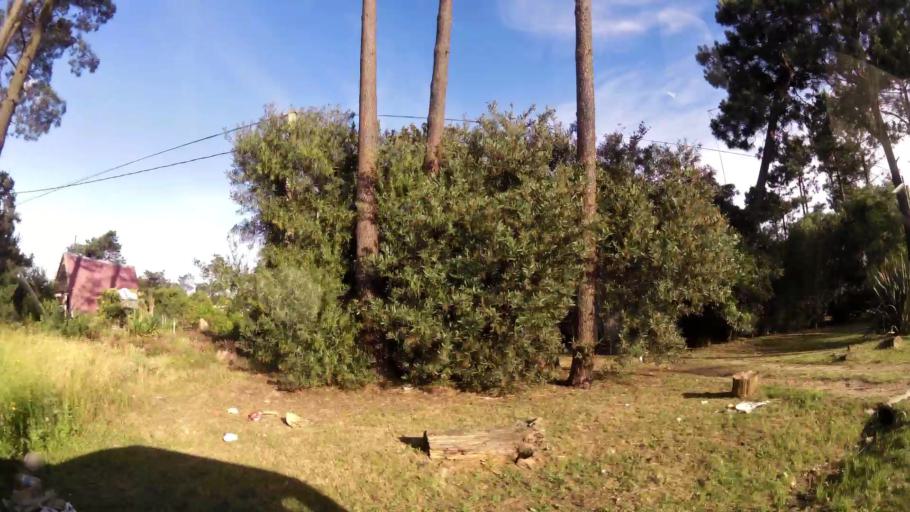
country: UY
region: Canelones
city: Empalme Olmos
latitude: -34.7683
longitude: -55.8620
